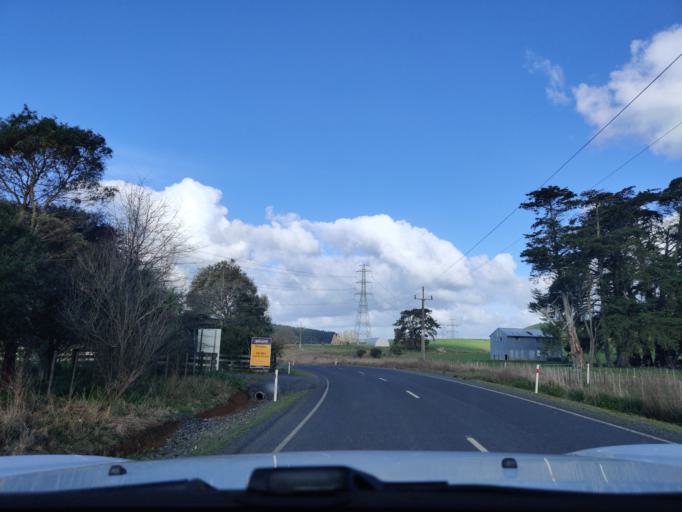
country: NZ
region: Waikato
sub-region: Waikato District
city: Te Kauwhata
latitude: -37.2898
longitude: 175.2199
